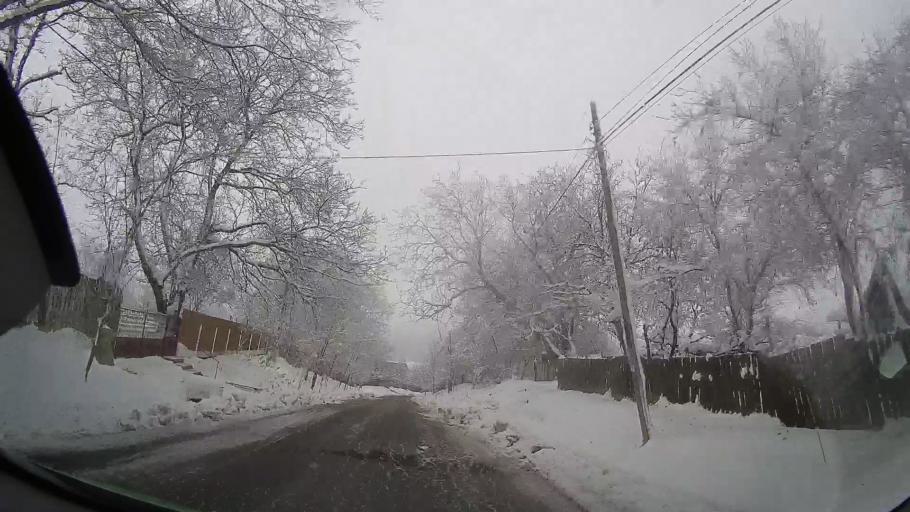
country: RO
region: Neamt
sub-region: Comuna Poenari
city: Poienari
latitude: 46.8892
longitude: 27.1335
